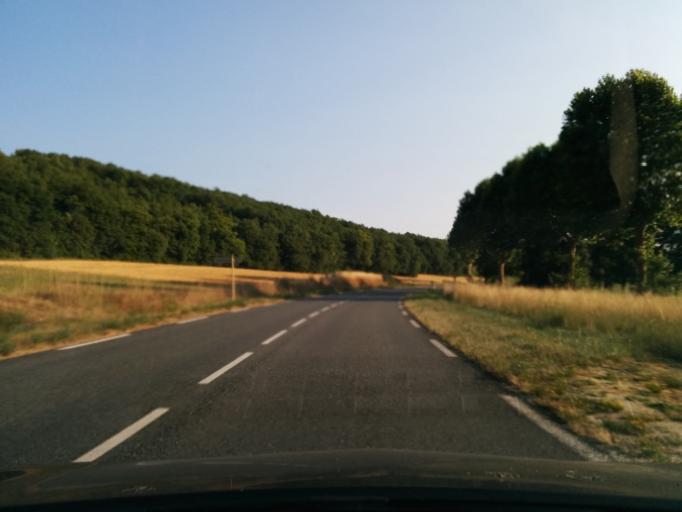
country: FR
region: Midi-Pyrenees
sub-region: Departement du Lot
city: Le Vigan
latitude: 44.6861
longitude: 1.4865
